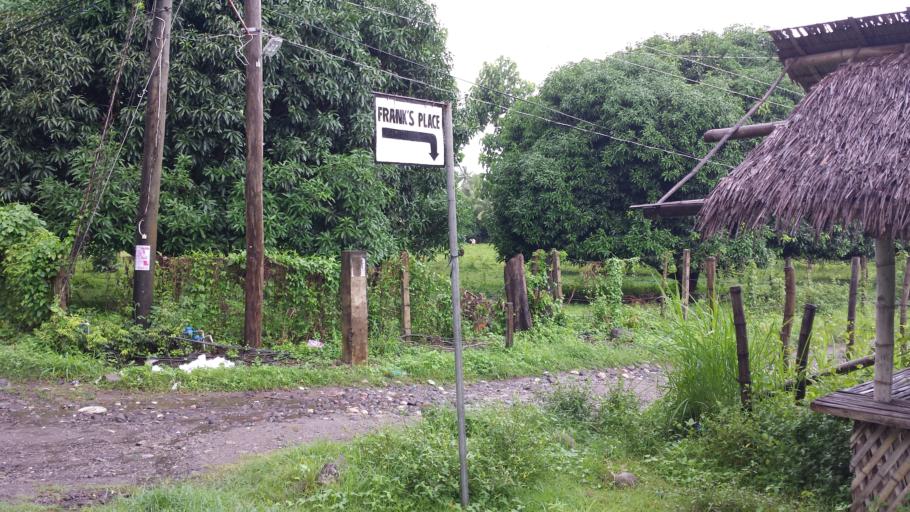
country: PH
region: Central Visayas
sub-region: Province of Negros Oriental
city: Maayong Tubig
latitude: 9.1639
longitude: 123.2435
